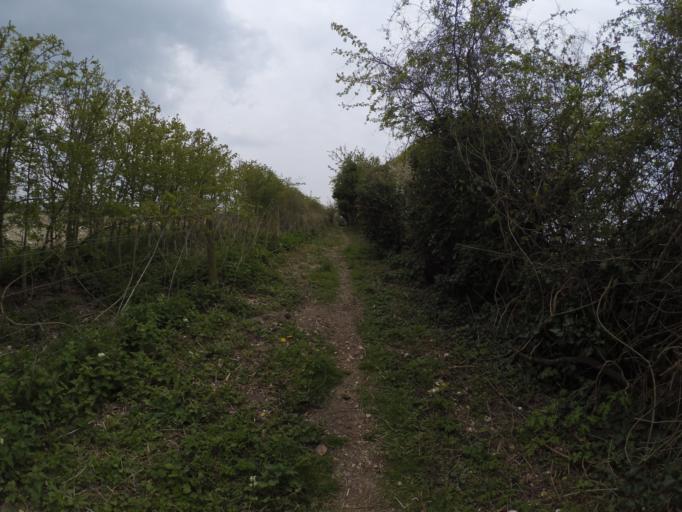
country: GB
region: England
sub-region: West Sussex
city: Arundel
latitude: 50.8824
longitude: -0.5229
